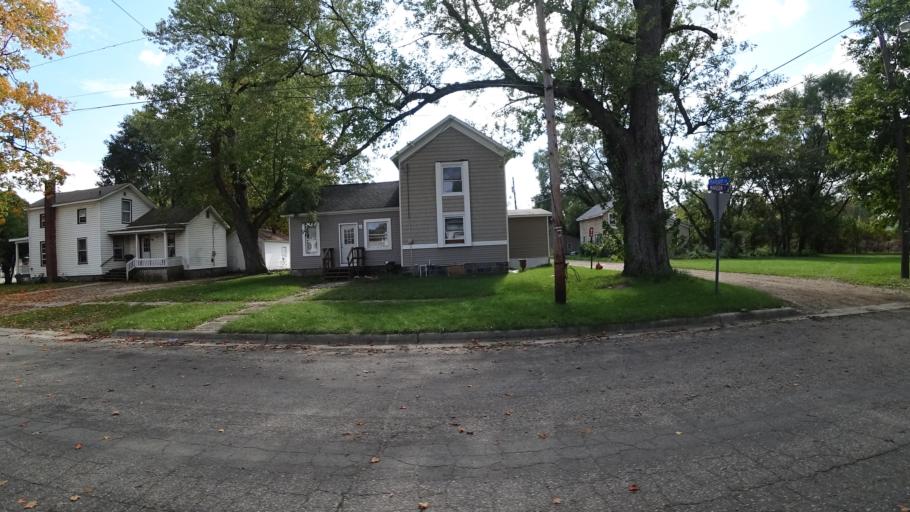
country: US
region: Michigan
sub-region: Saint Joseph County
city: Three Rivers
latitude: 41.9362
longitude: -85.6276
